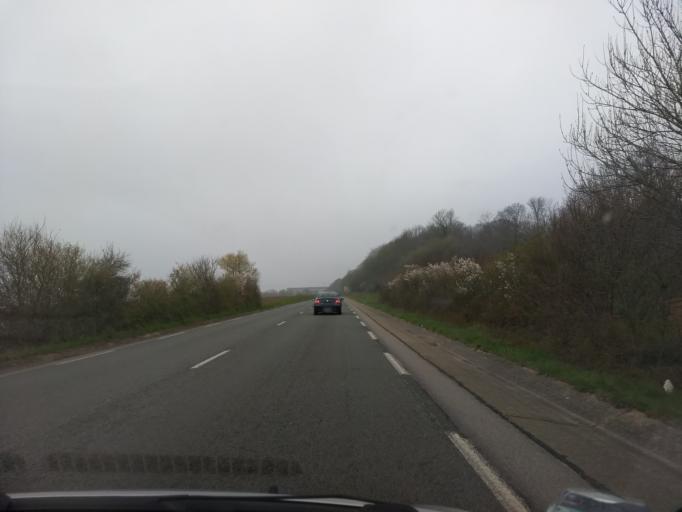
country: FR
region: Nord-Pas-de-Calais
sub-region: Departement du Pas-de-Calais
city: Verton
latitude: 50.4137
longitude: 1.6744
